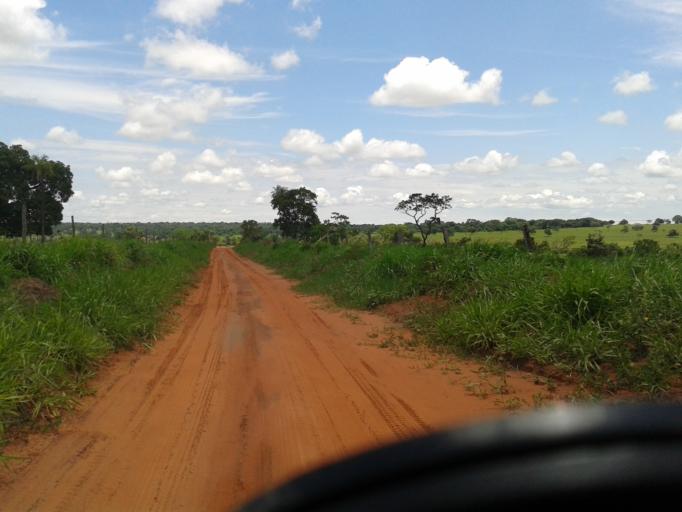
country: BR
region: Minas Gerais
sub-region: Santa Vitoria
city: Santa Vitoria
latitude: -18.9668
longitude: -49.8782
